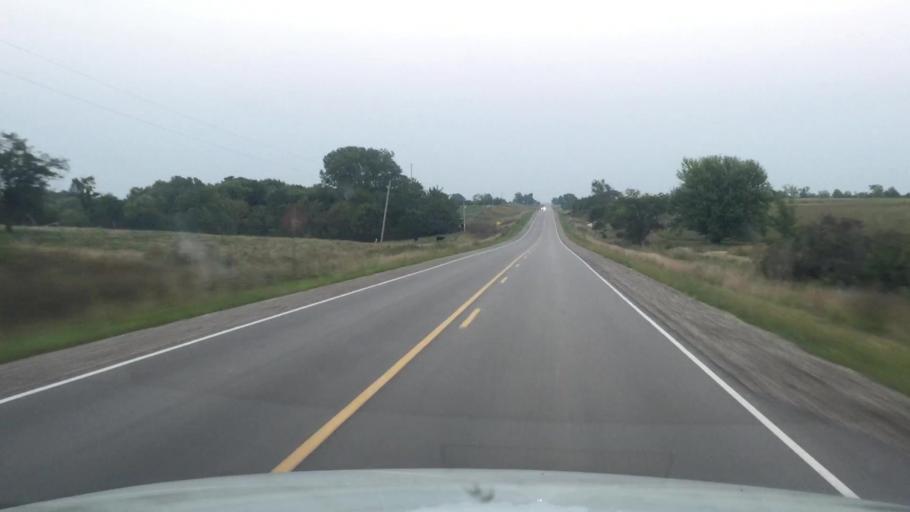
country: US
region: Iowa
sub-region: Marion County
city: Melcher-Dallas
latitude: 41.1895
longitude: -93.4215
